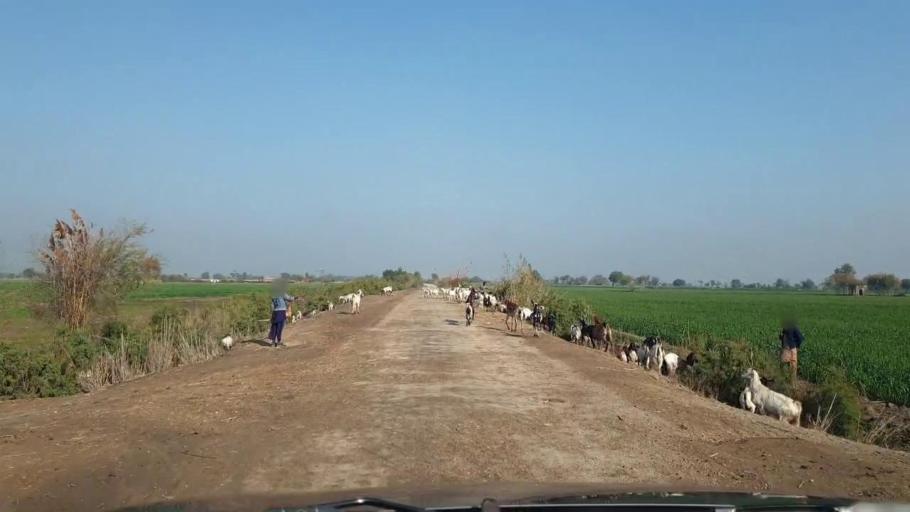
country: PK
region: Sindh
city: Sinjhoro
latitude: 26.0585
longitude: 68.7882
